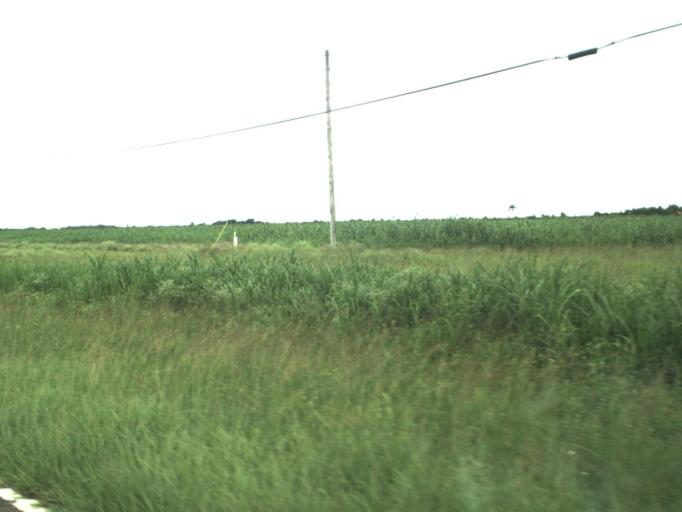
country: US
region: Florida
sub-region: Miami-Dade County
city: Florida City
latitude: 25.4142
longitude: -80.5170
